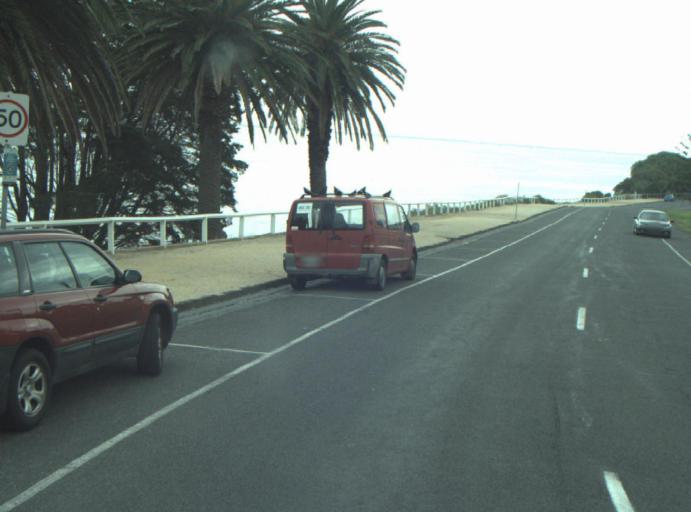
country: AU
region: Victoria
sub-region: Greater Geelong
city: East Geelong
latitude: -38.1472
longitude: 144.3750
